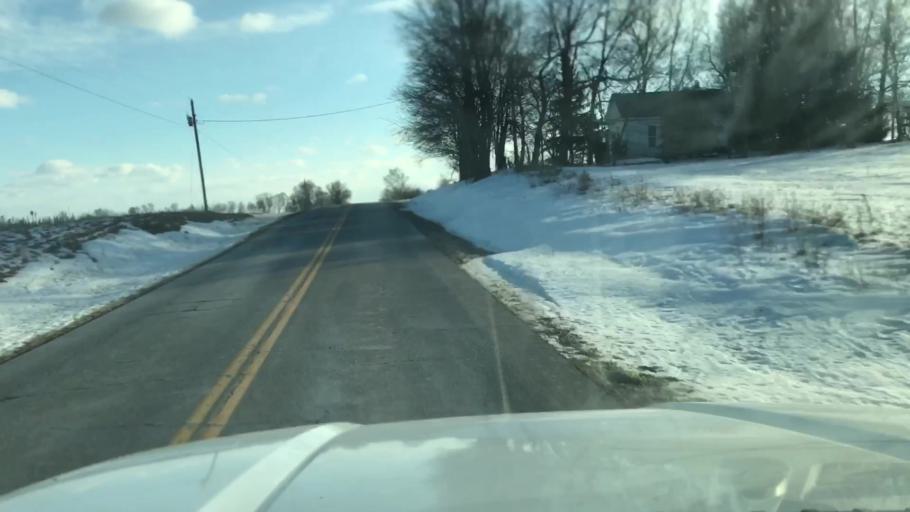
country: US
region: Missouri
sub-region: Andrew County
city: Savannah
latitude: 40.0507
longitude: -94.9750
